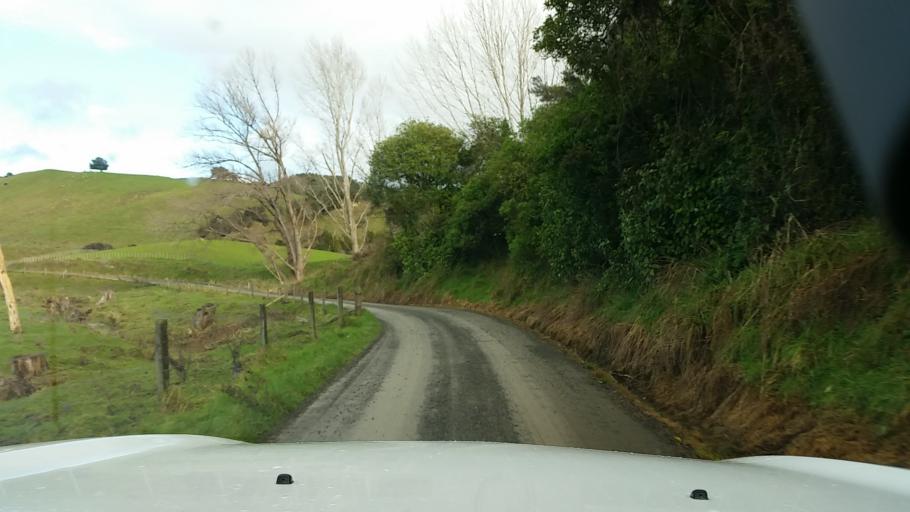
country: NZ
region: Wellington
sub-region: South Wairarapa District
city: Waipawa
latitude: -41.2144
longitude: 175.6042
